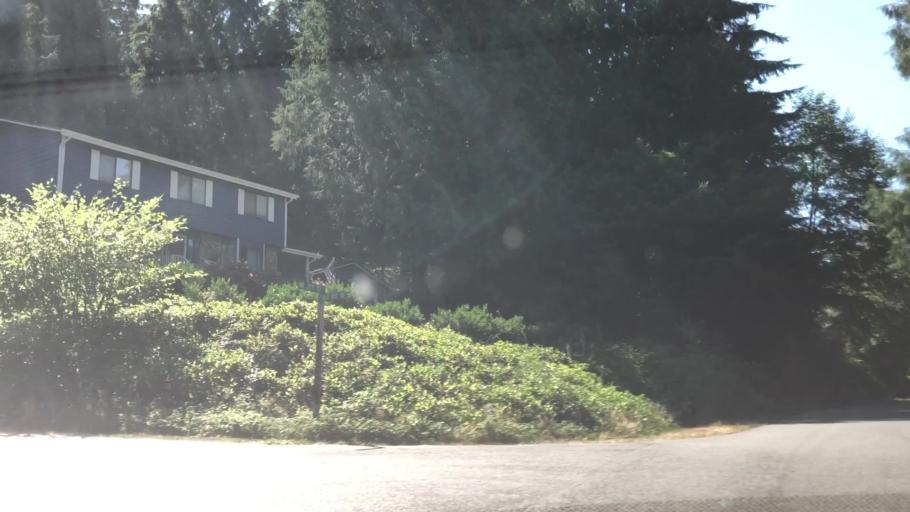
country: US
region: Washington
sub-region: King County
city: Cottage Lake
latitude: 47.7577
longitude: -122.0936
